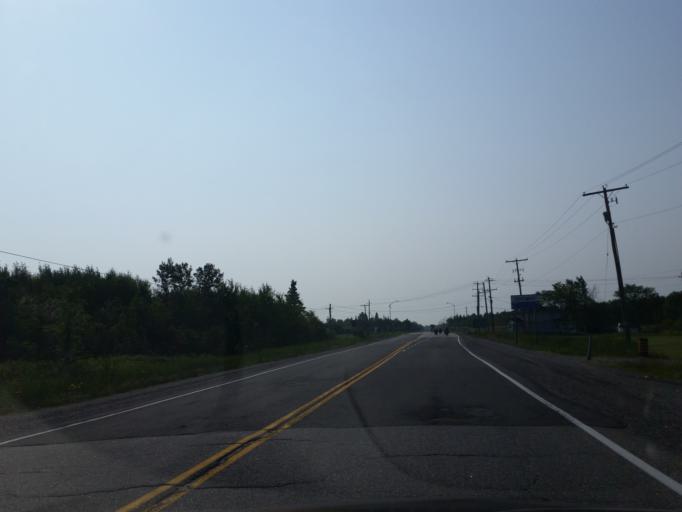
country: CA
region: Ontario
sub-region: Nipissing District
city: North Bay
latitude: 46.3793
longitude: -79.9762
